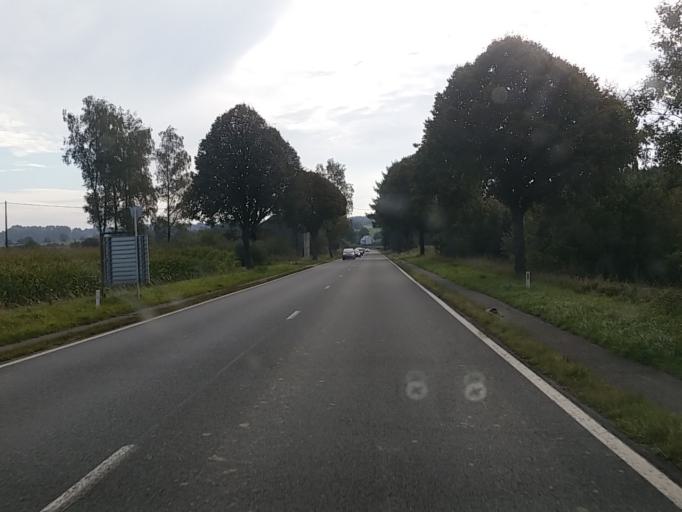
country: BE
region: Wallonia
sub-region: Province du Luxembourg
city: Florenville
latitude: 49.6894
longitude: 5.3453
